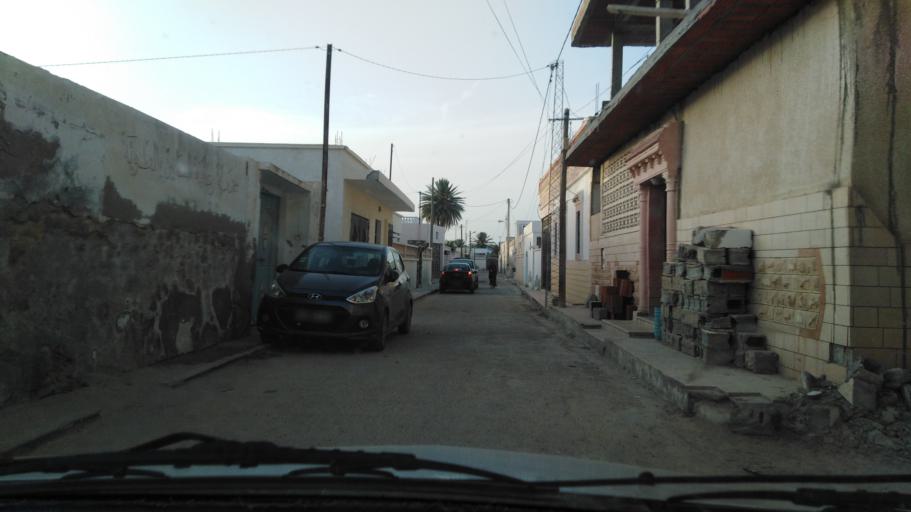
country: TN
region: Qabis
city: Gabes
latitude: 33.9569
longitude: 9.9979
